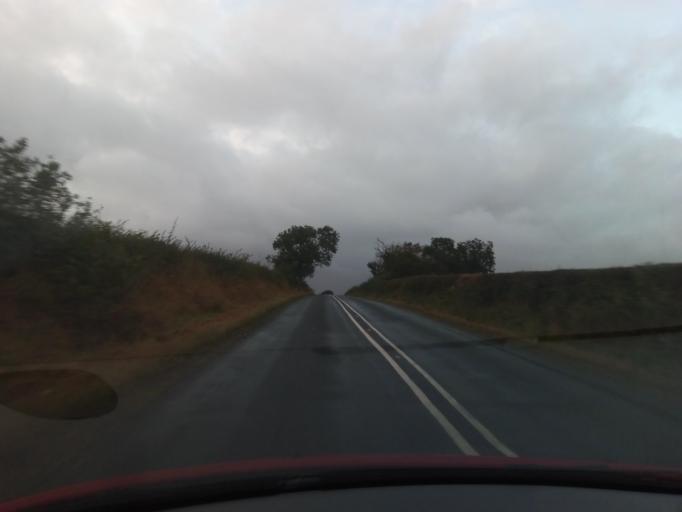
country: GB
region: England
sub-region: Darlington
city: Summerhouse
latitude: 54.5986
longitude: -1.6807
